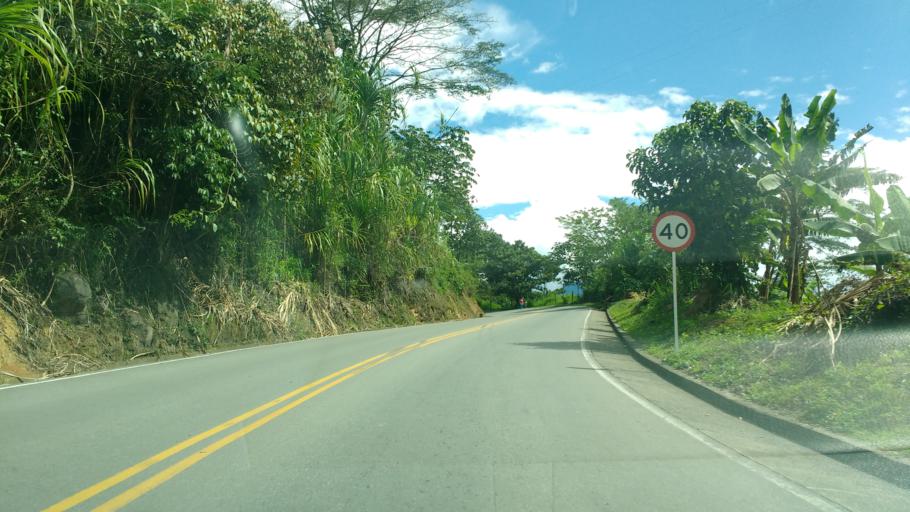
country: CO
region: Antioquia
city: Titiribi
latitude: 6.0487
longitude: -75.7576
